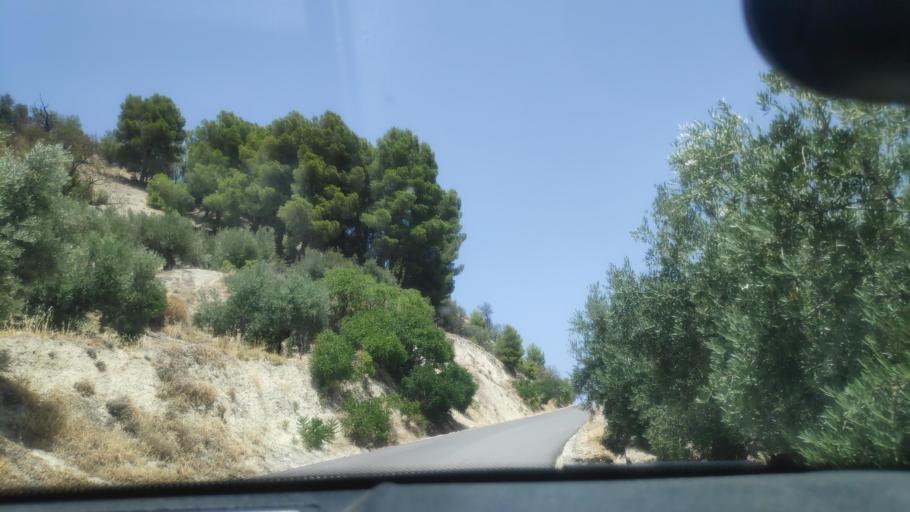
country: ES
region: Andalusia
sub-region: Provincia de Jaen
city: Torres
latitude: 37.7907
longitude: -3.4620
